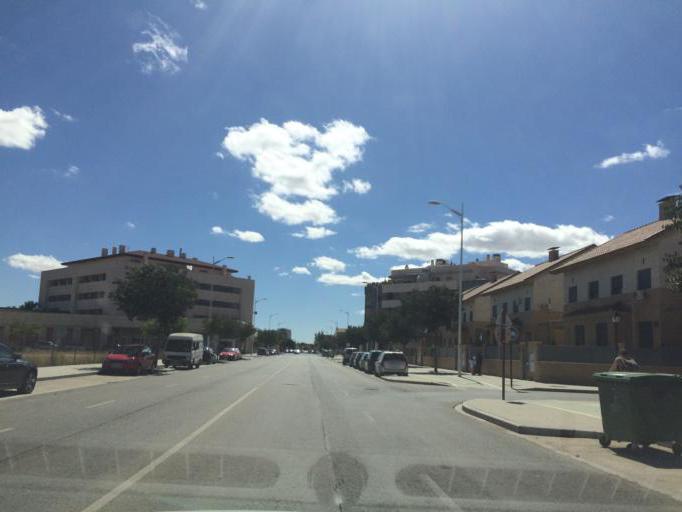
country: ES
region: Castille-La Mancha
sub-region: Provincia de Albacete
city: Albacete
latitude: 38.9840
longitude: -1.8423
